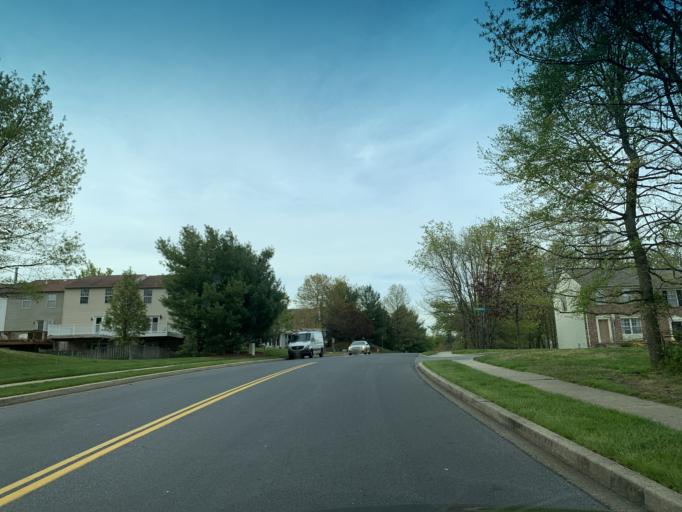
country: US
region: Maryland
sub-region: Harford County
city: Riverside
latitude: 39.4781
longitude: -76.2542
